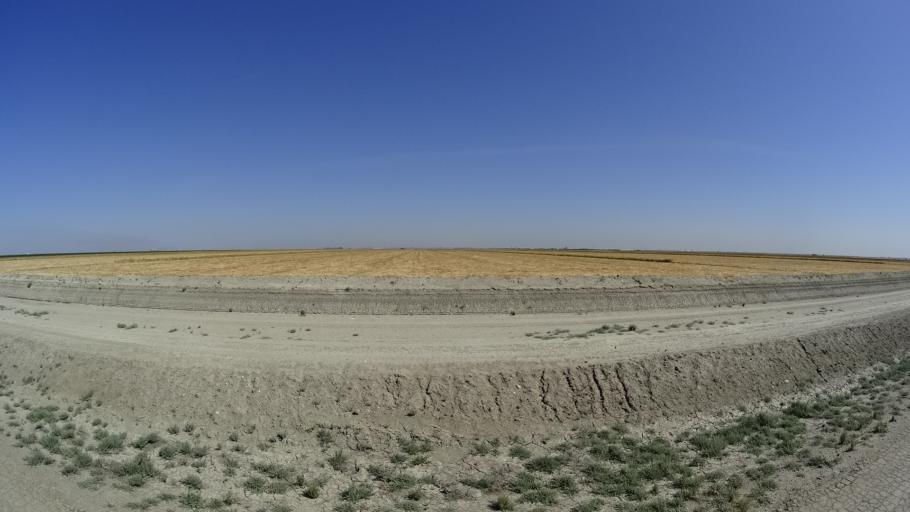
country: US
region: California
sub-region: Tulare County
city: Alpaugh
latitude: 35.9781
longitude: -119.5599
